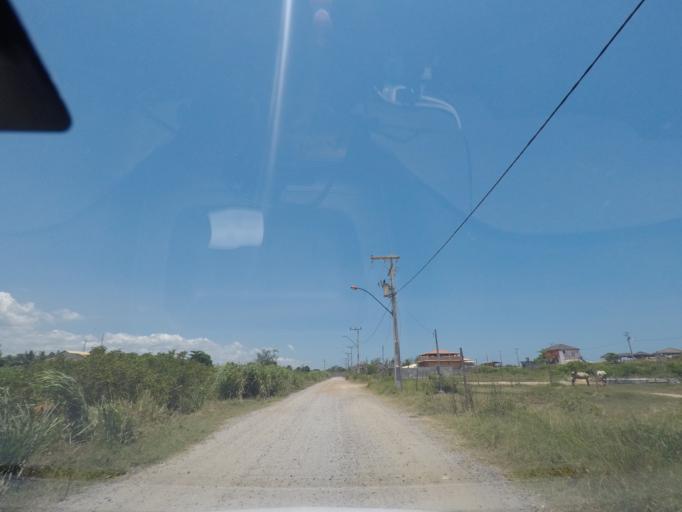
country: BR
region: Rio de Janeiro
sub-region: Niteroi
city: Niteroi
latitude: -22.9680
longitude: -42.9898
